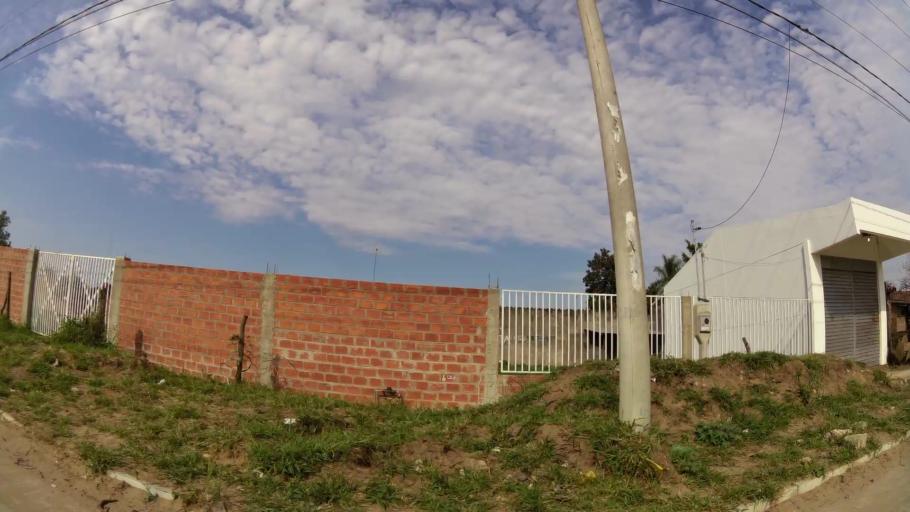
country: BO
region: Santa Cruz
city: Santa Cruz de la Sierra
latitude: -17.7294
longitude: -63.1333
